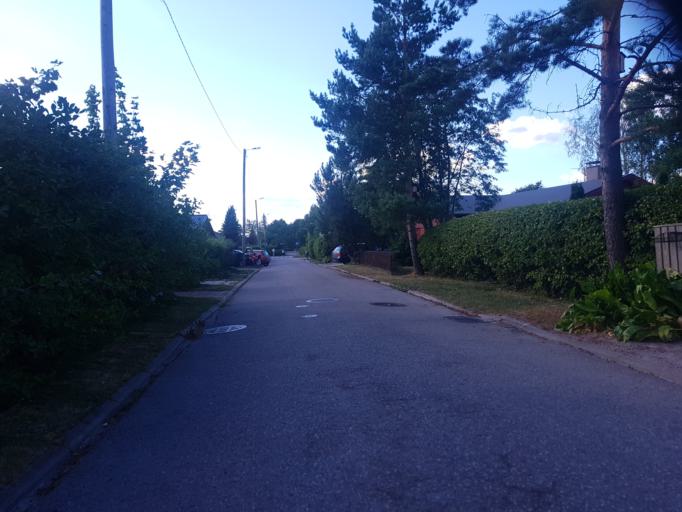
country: FI
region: Uusimaa
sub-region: Helsinki
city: Vantaa
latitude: 60.2829
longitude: 25.0042
